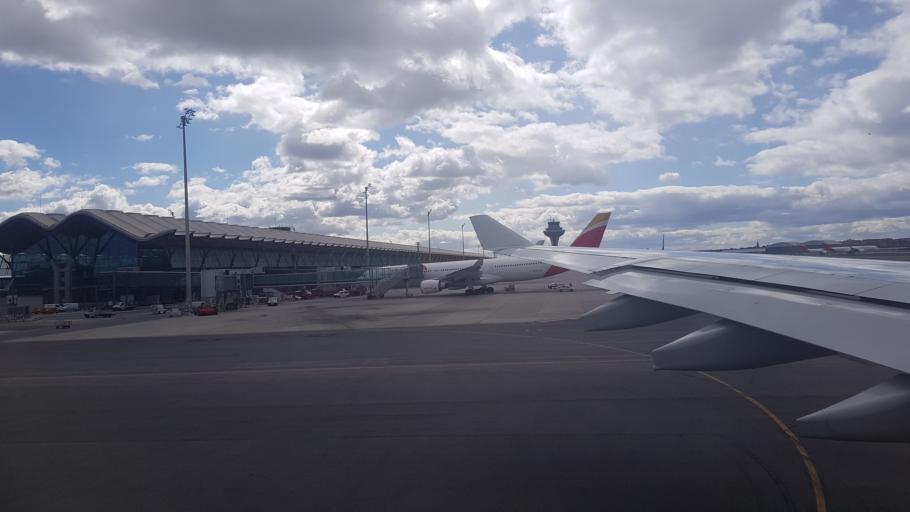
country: ES
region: Madrid
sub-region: Provincia de Madrid
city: Barajas de Madrid
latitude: 40.5003
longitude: -3.5691
